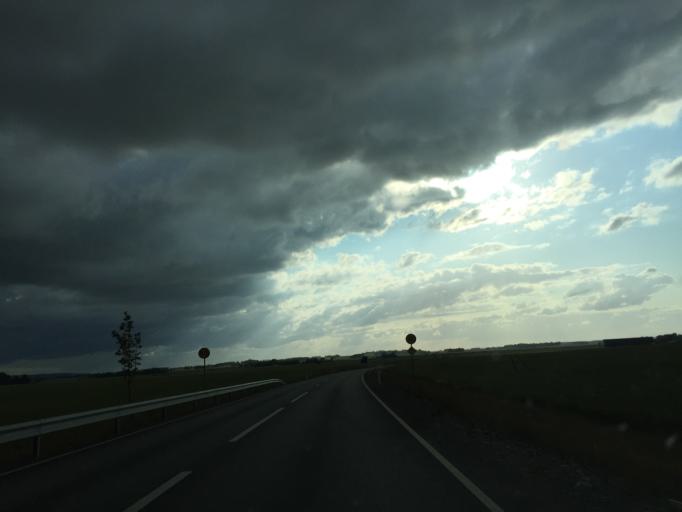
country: SE
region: OEstergoetland
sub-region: Vadstena Kommun
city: Vadstena
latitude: 58.4341
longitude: 14.8968
